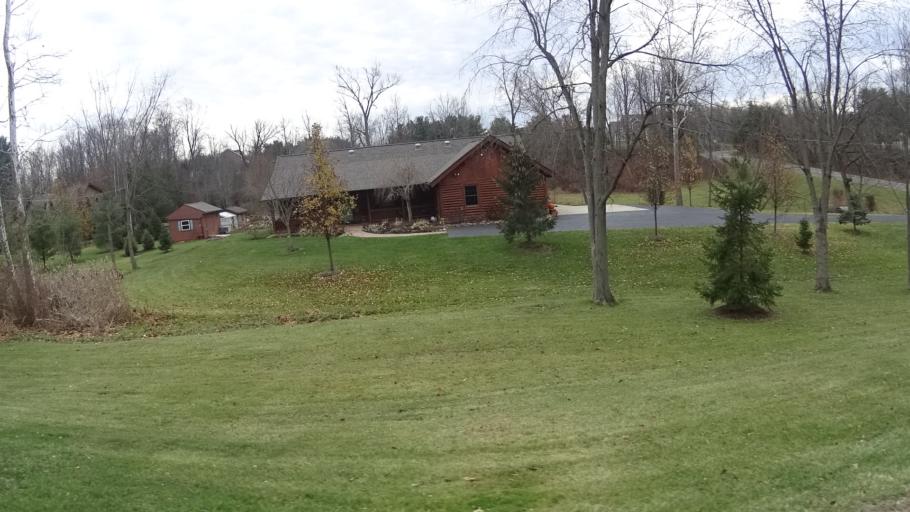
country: US
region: Ohio
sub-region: Medina County
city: Brunswick
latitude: 41.2749
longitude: -81.8972
